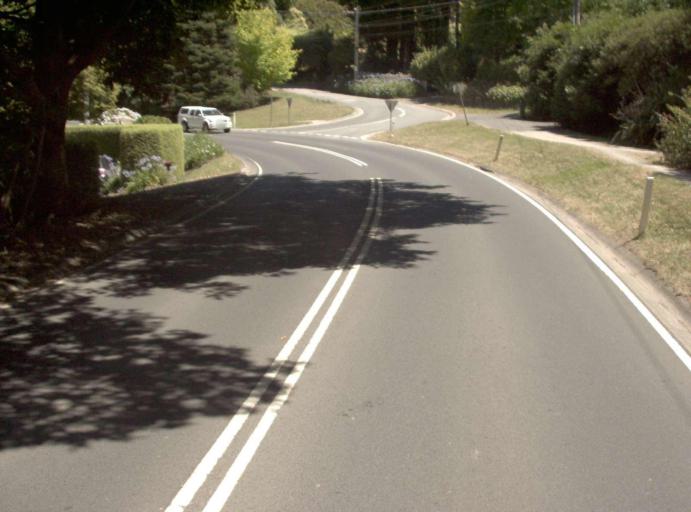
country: AU
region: Victoria
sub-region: Yarra Ranges
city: Ferny Creek
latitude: -37.8788
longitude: 145.3408
